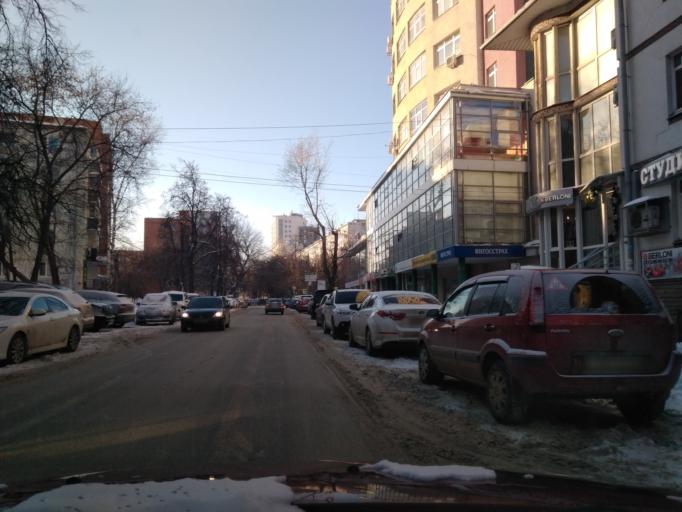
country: RU
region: Nizjnij Novgorod
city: Nizhniy Novgorod
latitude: 56.3191
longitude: 44.0220
